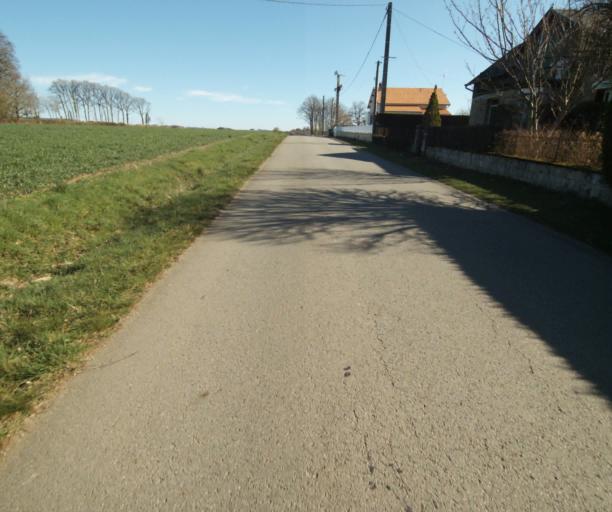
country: FR
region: Limousin
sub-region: Departement de la Correze
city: Chamboulive
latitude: 45.4787
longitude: 1.7125
